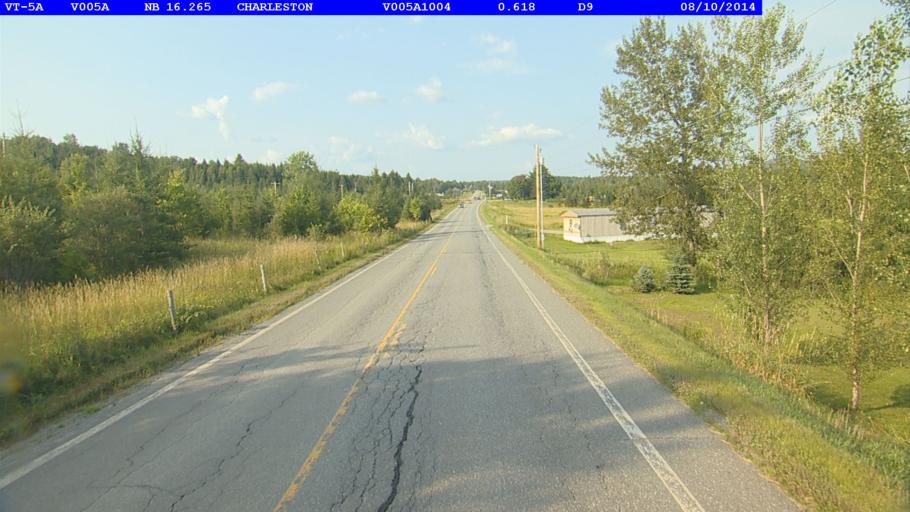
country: US
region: Vermont
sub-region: Orleans County
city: Newport
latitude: 44.8428
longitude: -72.0603
